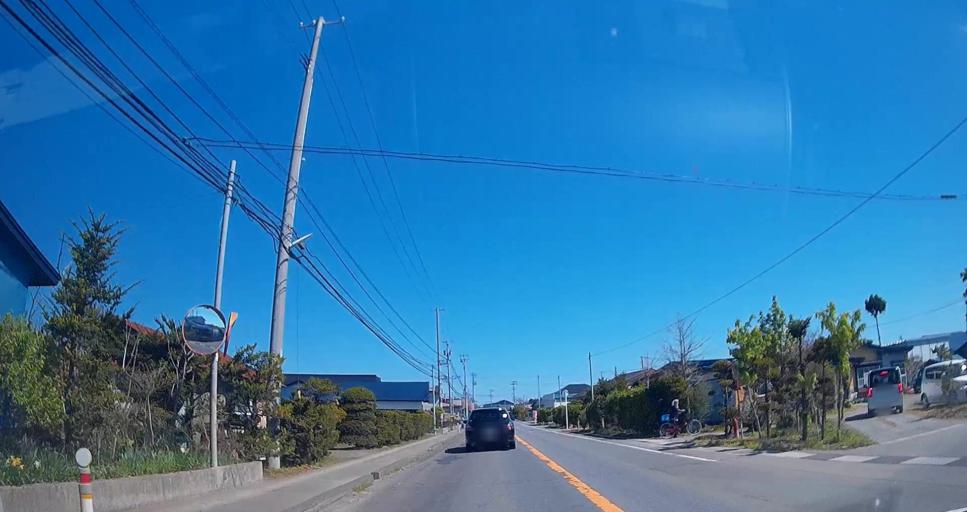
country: JP
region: Aomori
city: Misawa
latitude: 40.7867
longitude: 141.3996
